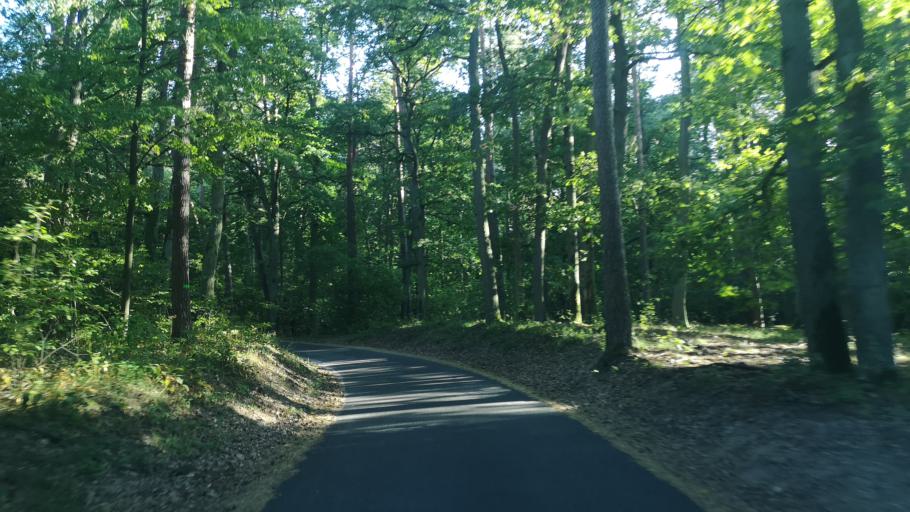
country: PL
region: Kujawsko-Pomorskie
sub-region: Powiat swiecki
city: Warlubie
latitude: 53.4776
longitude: 18.6318
